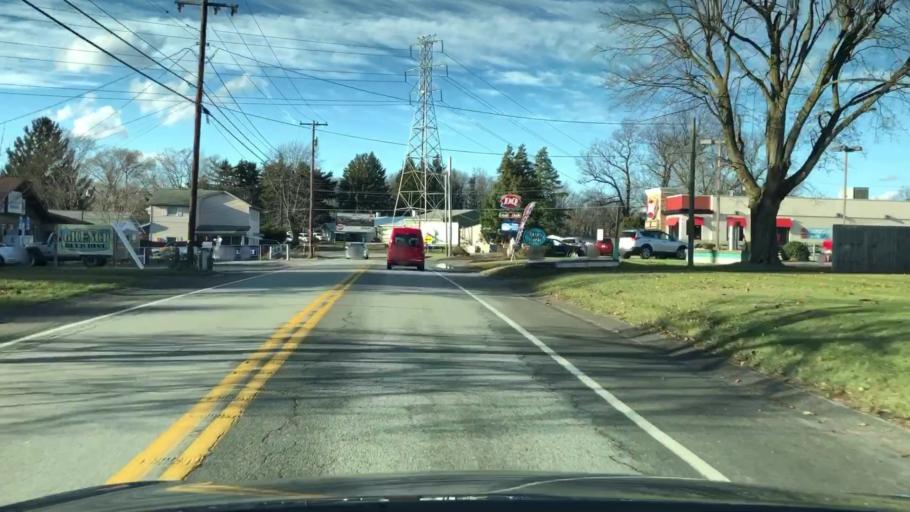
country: US
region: Pennsylvania
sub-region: Butler County
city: Meadowood
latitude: 40.8421
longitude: -79.8726
